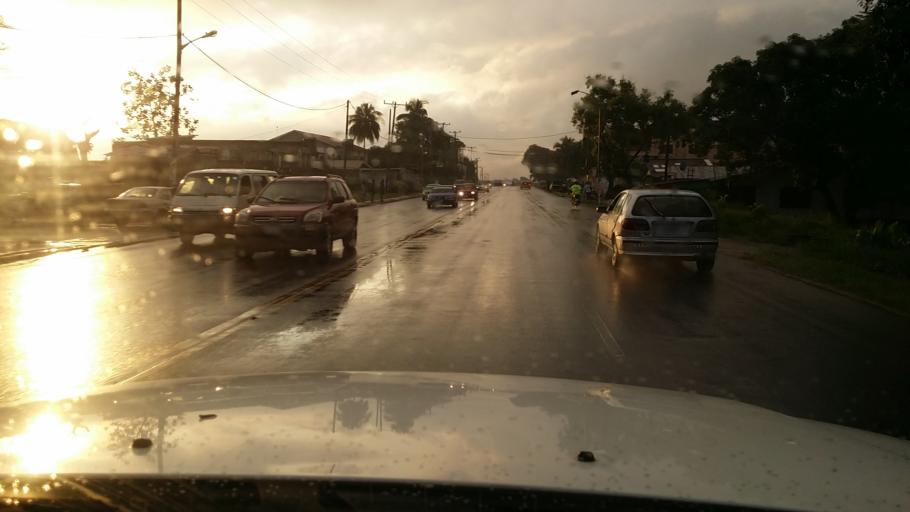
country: LR
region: Montserrado
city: Monrovia
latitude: 6.2667
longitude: -10.7220
